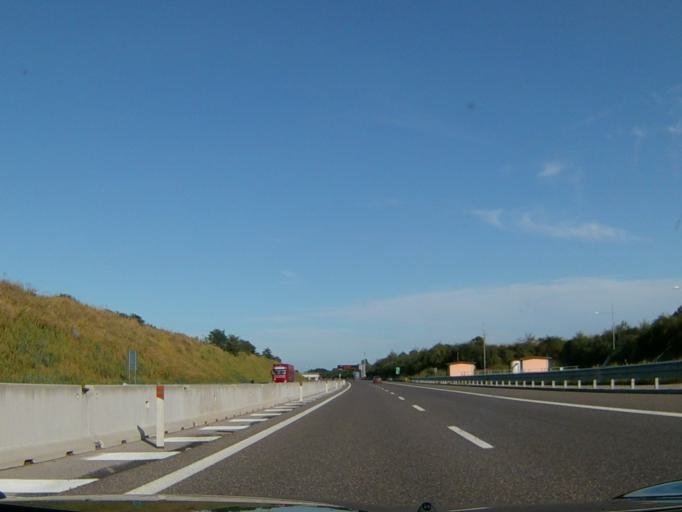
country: IT
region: Lombardy
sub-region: Provincia di Brescia
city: Castenedolo
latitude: 45.4551
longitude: 10.2653
